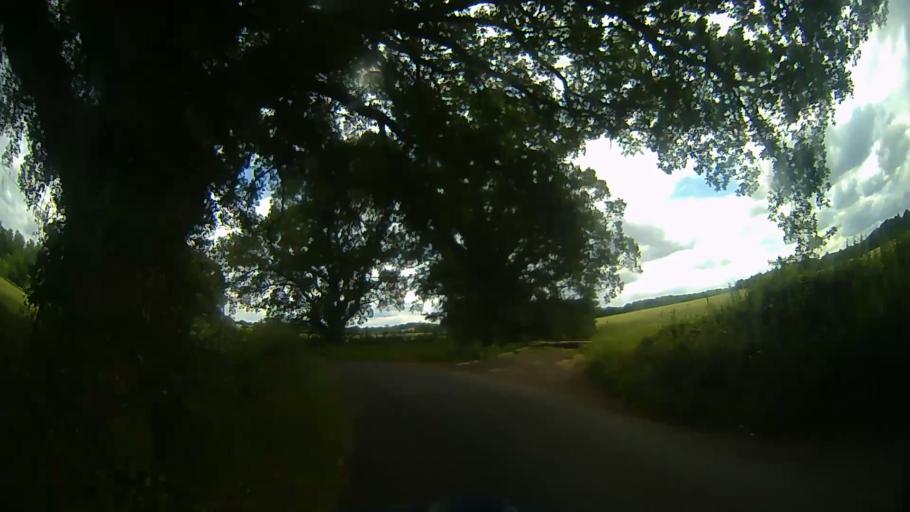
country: GB
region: England
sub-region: Hampshire
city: Basingstoke
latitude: 51.3084
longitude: -1.0650
